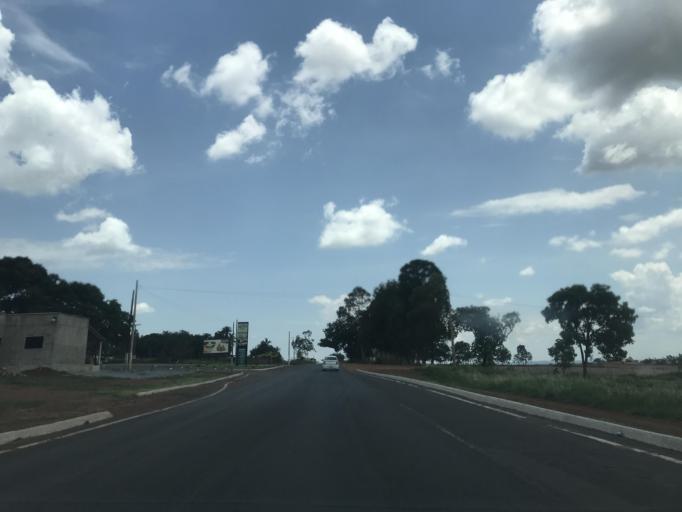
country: BR
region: Goias
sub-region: Bela Vista De Goias
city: Bela Vista de Goias
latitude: -17.0698
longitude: -48.6575
